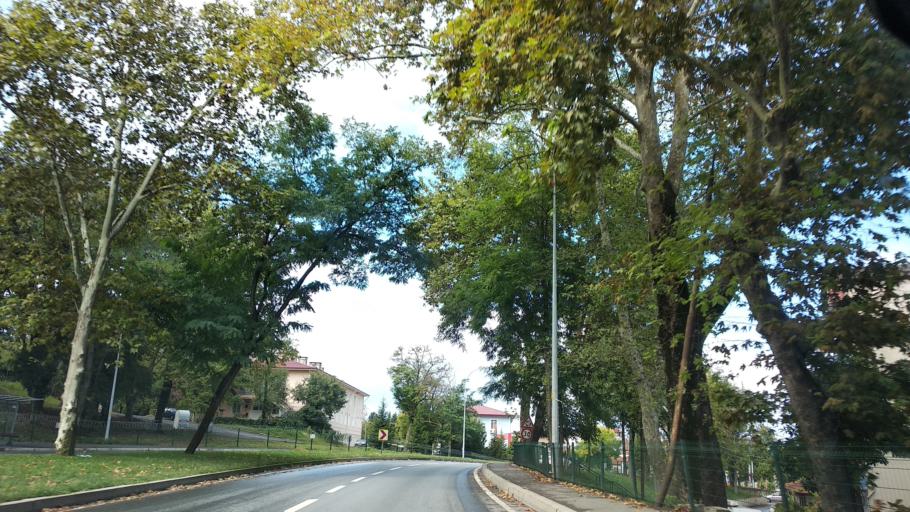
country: TR
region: Sakarya
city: Adapazari
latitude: 40.7565
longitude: 30.3745
